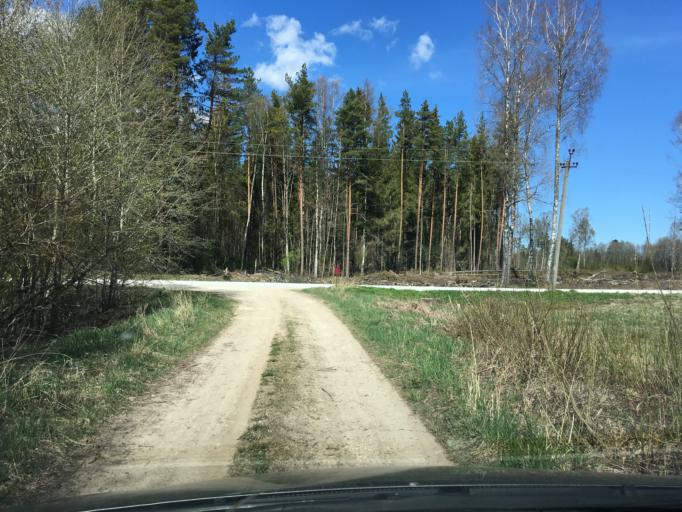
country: EE
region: Harju
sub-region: Raasiku vald
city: Arukula
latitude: 59.2096
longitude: 25.1176
